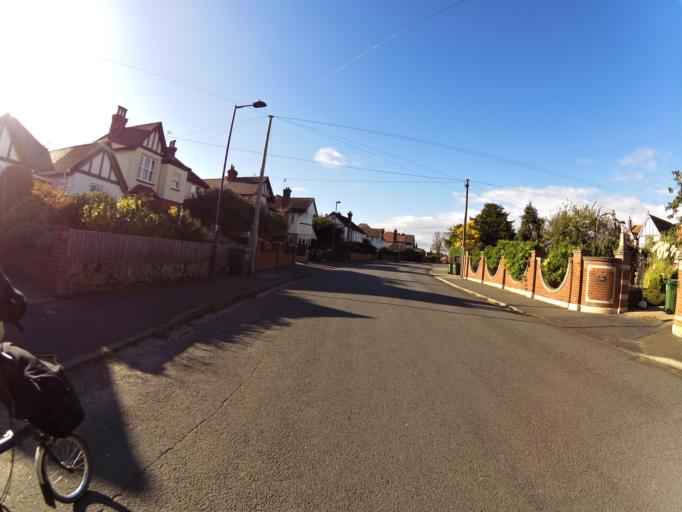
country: GB
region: England
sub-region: Suffolk
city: Felixstowe
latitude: 51.9663
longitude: 1.3589
